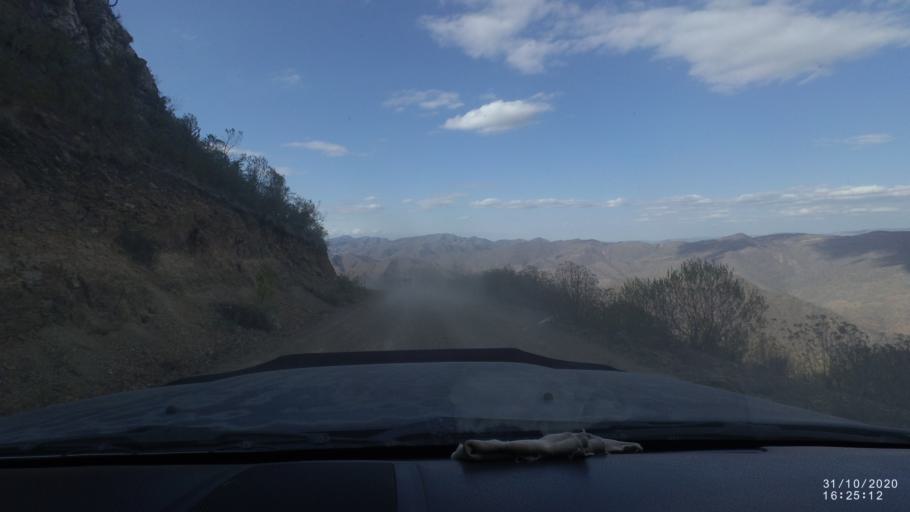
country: BO
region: Chuquisaca
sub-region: Provincia Zudanez
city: Mojocoya
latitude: -18.4025
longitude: -64.5875
